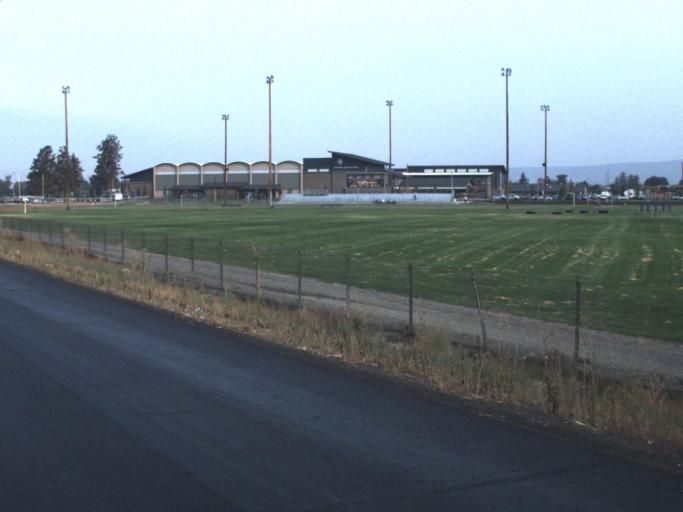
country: US
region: Washington
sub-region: Yakima County
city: Wapato
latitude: 46.4346
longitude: -120.4200
